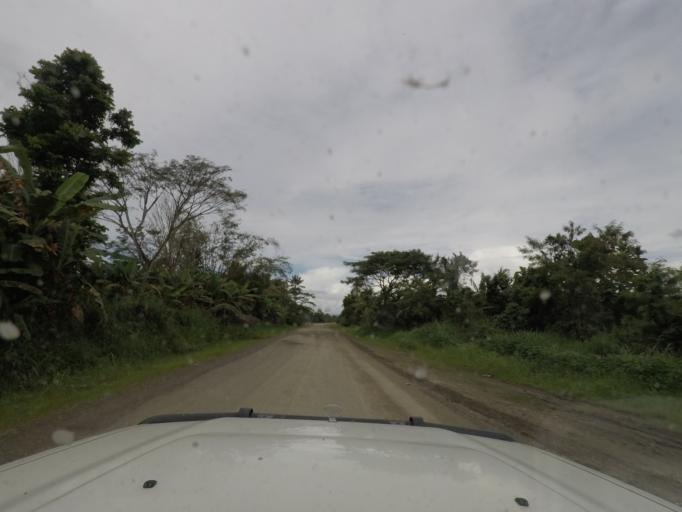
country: PG
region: Eastern Highlands
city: Goroka
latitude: -5.6592
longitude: 145.4983
